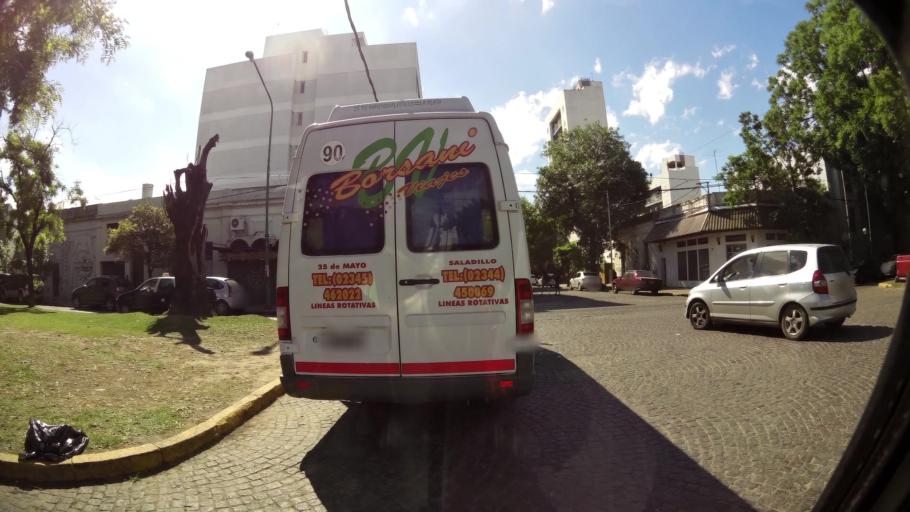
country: AR
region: Buenos Aires
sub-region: Partido de La Plata
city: La Plata
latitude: -34.9251
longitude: -57.9337
